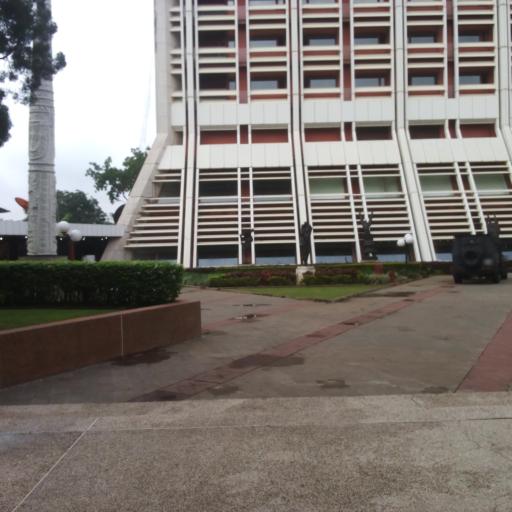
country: NG
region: Abuja Federal Capital Territory
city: Abuja
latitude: 9.0746
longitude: 7.4956
